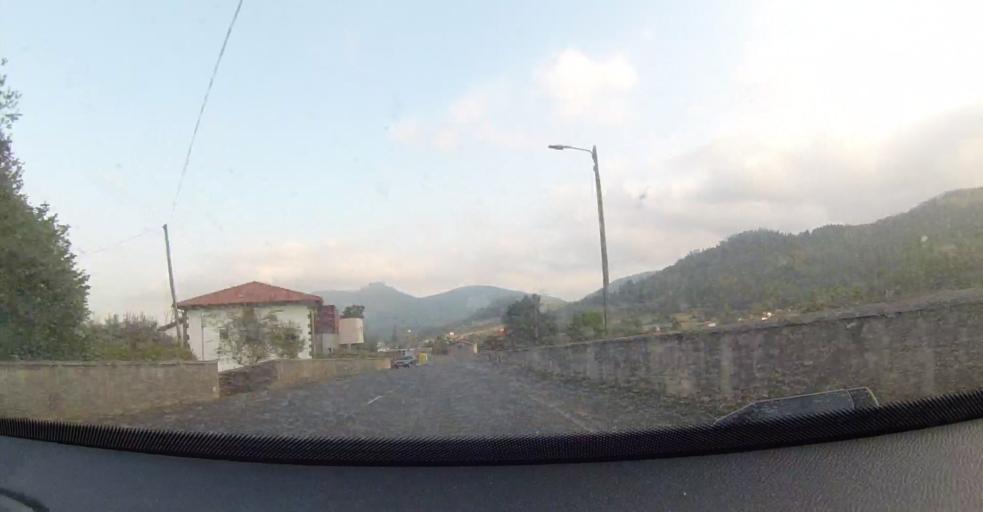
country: ES
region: Basque Country
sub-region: Bizkaia
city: Sopuerta
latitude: 43.2810
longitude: -3.1608
